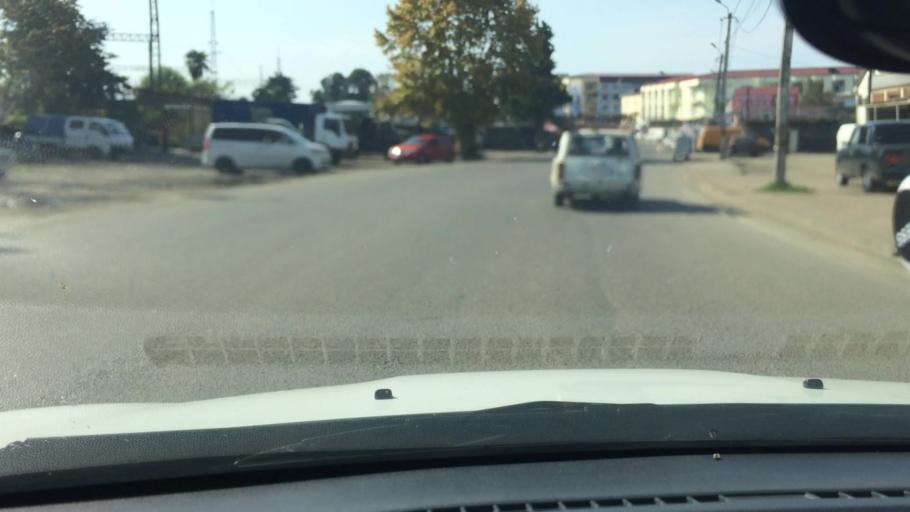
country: GE
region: Ajaria
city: Kobuleti
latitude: 41.8121
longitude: 41.7819
